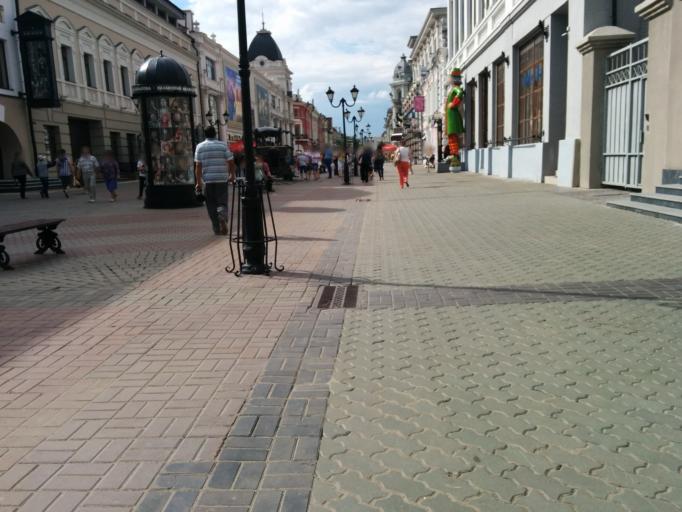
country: RU
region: Tatarstan
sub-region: Gorod Kazan'
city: Kazan
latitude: 55.7913
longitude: 49.1138
